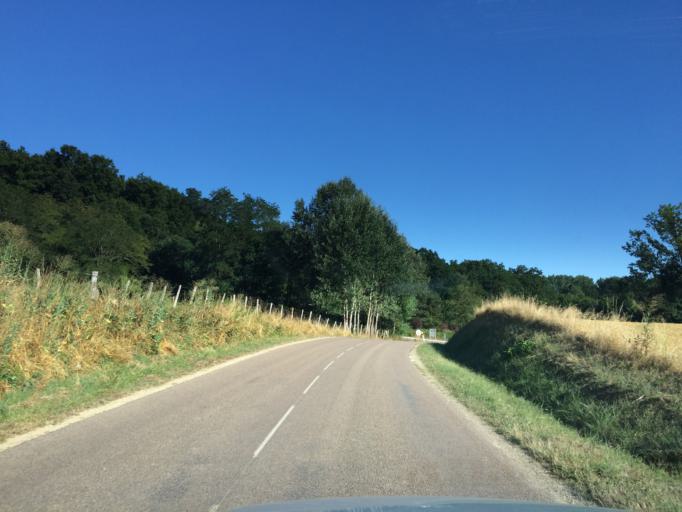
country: FR
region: Bourgogne
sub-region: Departement de l'Yonne
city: Fleury-la-Vallee
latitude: 47.8880
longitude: 3.4361
